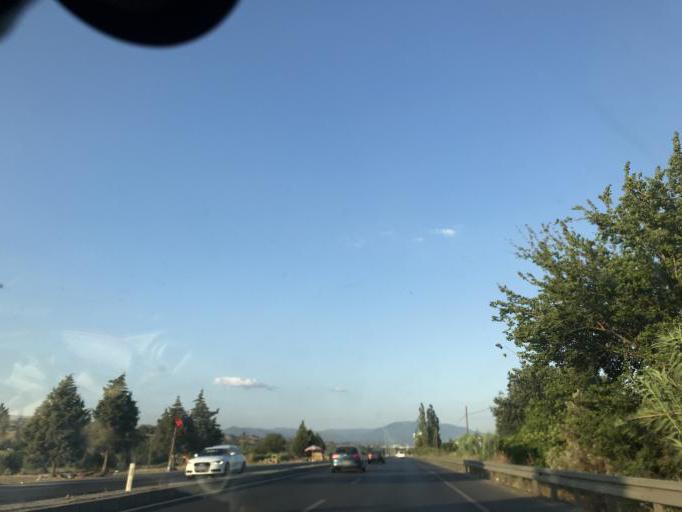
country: TR
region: Aydin
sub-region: Sultanhisar Ilcesi
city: Atca
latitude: 37.8876
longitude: 28.2260
